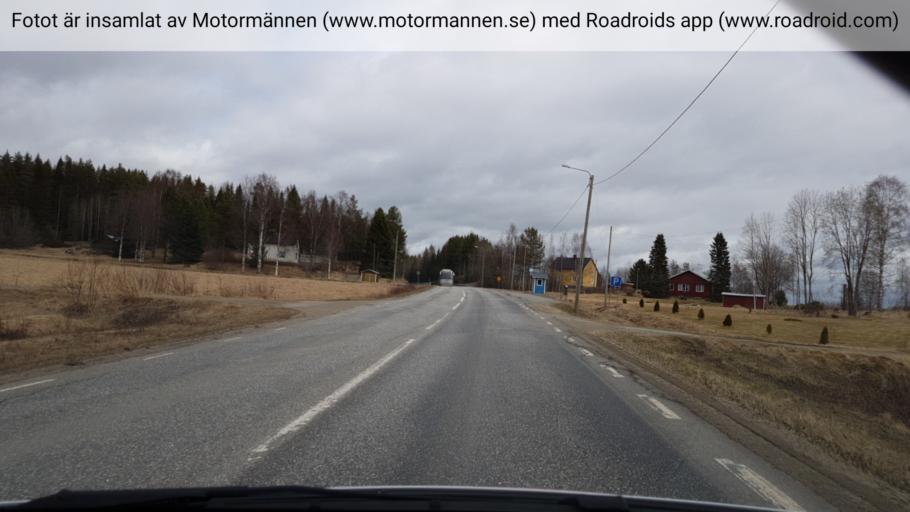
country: SE
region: Vaesterbotten
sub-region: Bjurholms Kommun
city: Bjurholm
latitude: 63.9162
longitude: 19.1745
